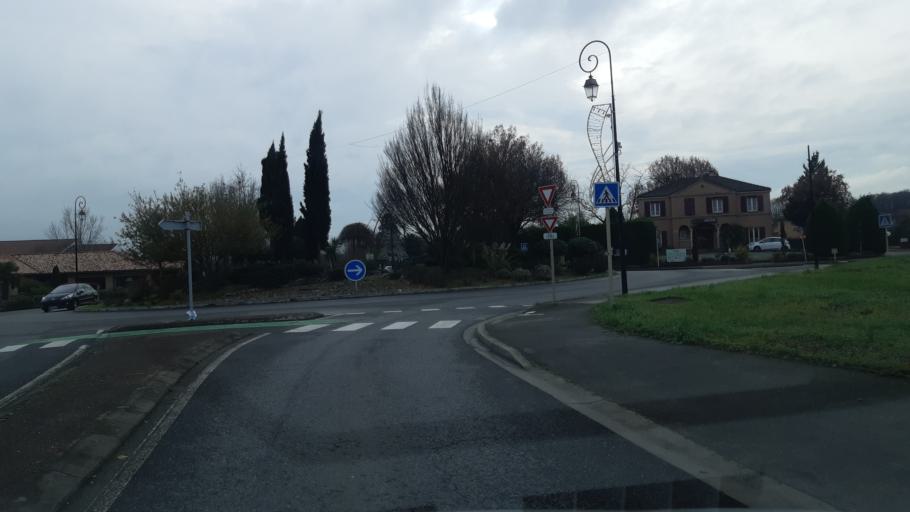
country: FR
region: Midi-Pyrenees
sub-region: Departement de la Haute-Garonne
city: Pibrac
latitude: 43.6106
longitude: 1.2846
